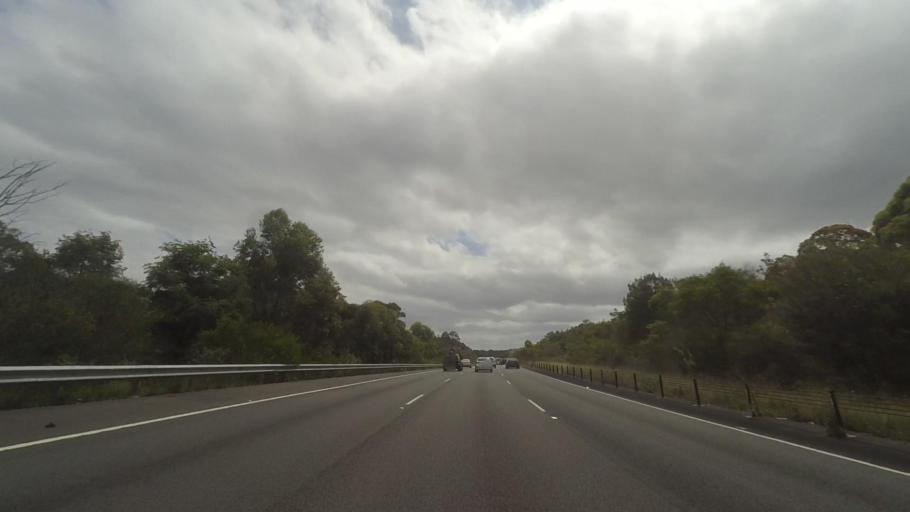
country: AU
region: New South Wales
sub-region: Gosford Shire
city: Point Clare
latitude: -33.4513
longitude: 151.2149
